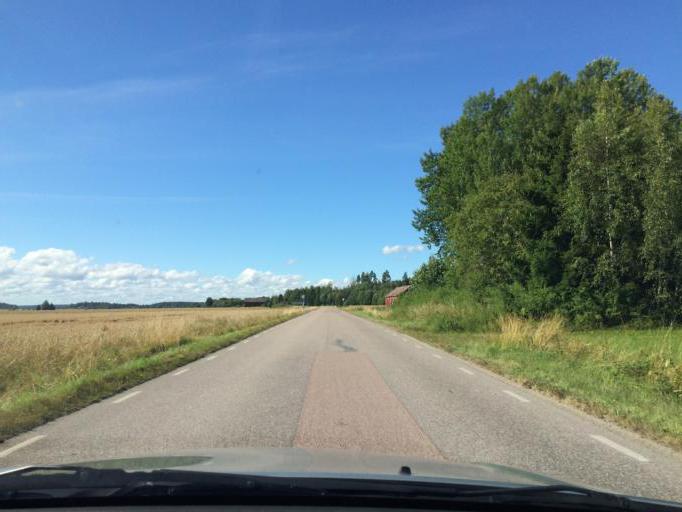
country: SE
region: Vaestmanland
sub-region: Vasteras
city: Vasteras
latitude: 59.5612
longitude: 16.4754
